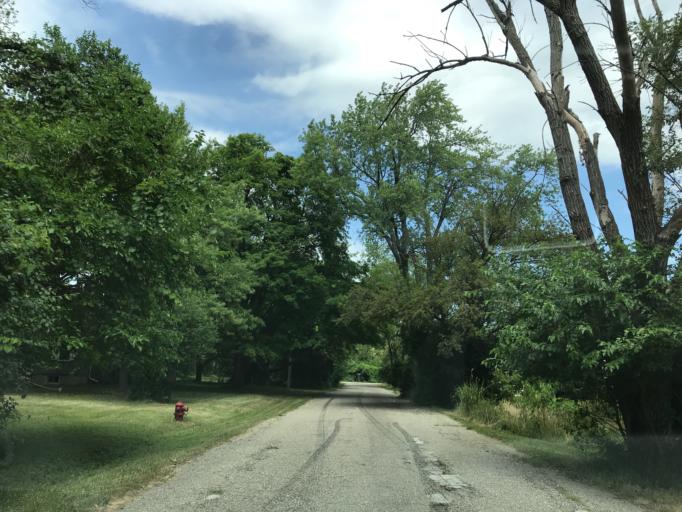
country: US
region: Michigan
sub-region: Oakland County
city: Bingham Farms
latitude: 42.4775
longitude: -83.2642
